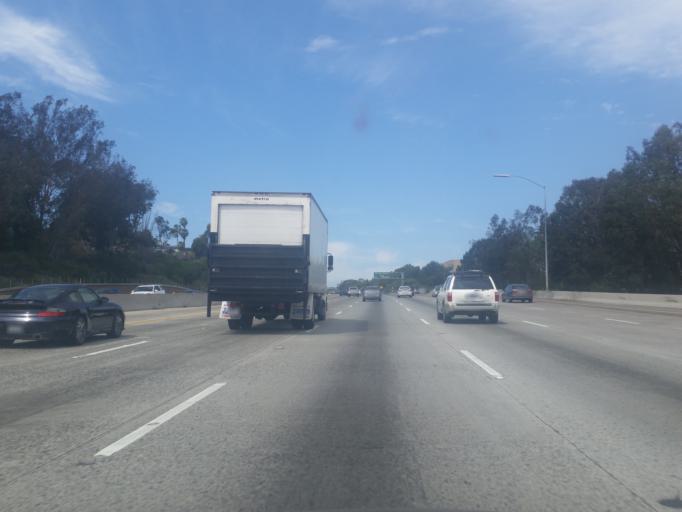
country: US
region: California
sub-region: San Diego County
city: Del Mar
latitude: 32.9373
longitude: -117.2415
